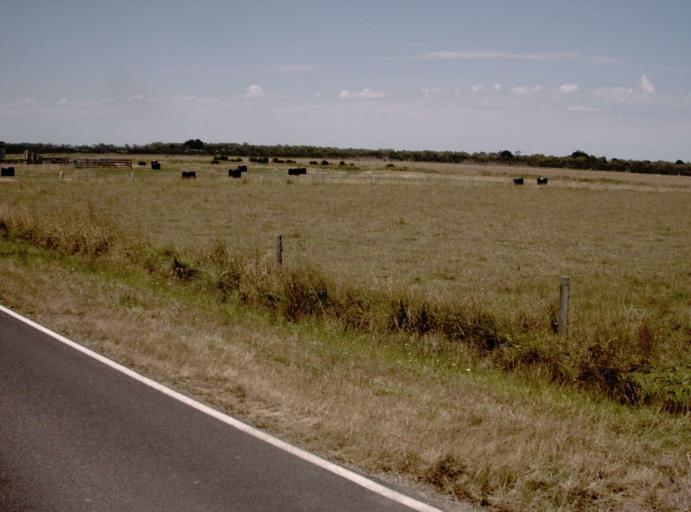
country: AU
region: Victoria
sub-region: Bass Coast
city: North Wonthaggi
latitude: -38.6911
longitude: 145.8751
